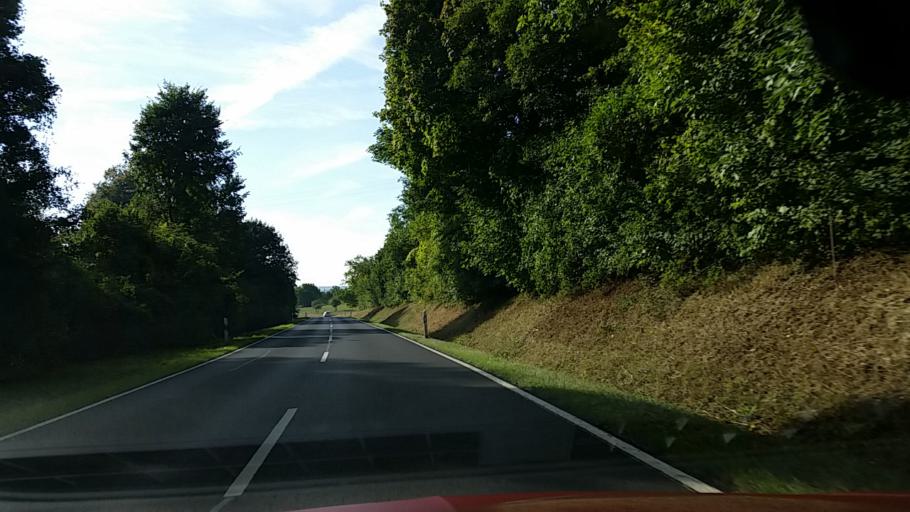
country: DE
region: Bavaria
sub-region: Regierungsbezirk Unterfranken
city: Himmelstadt
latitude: 49.9094
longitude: 9.7998
